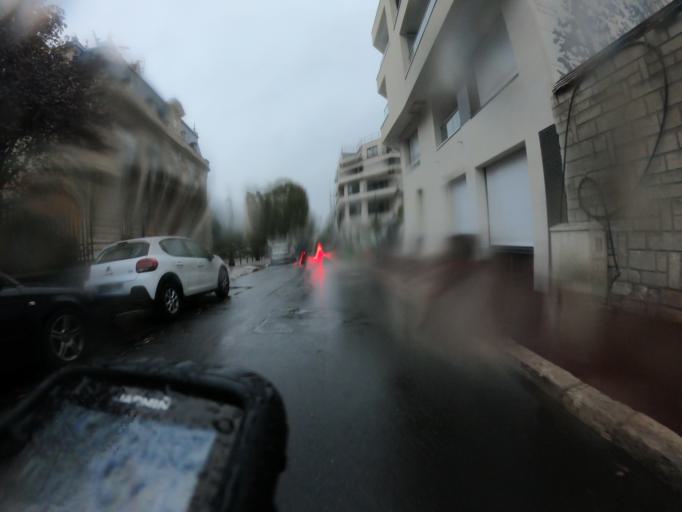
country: FR
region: Ile-de-France
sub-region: Departement des Hauts-de-Seine
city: Vanves
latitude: 48.8213
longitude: 2.2900
